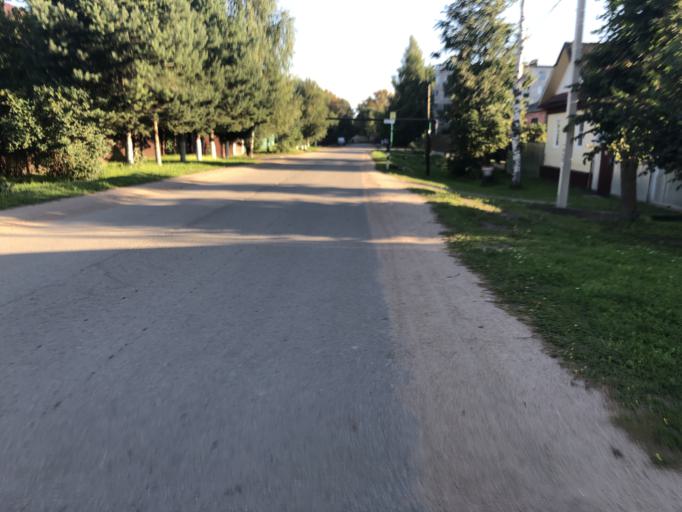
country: RU
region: Tverskaya
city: Rzhev
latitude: 56.2443
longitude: 34.3344
